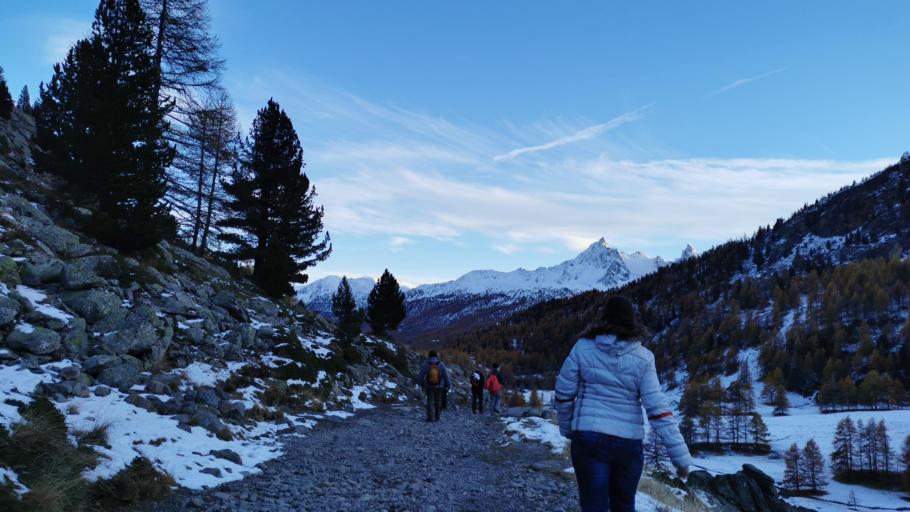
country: FR
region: Provence-Alpes-Cote d'Azur
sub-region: Departement des Hautes-Alpes
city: Le Monetier-les-Bains
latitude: 45.0647
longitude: 6.5213
